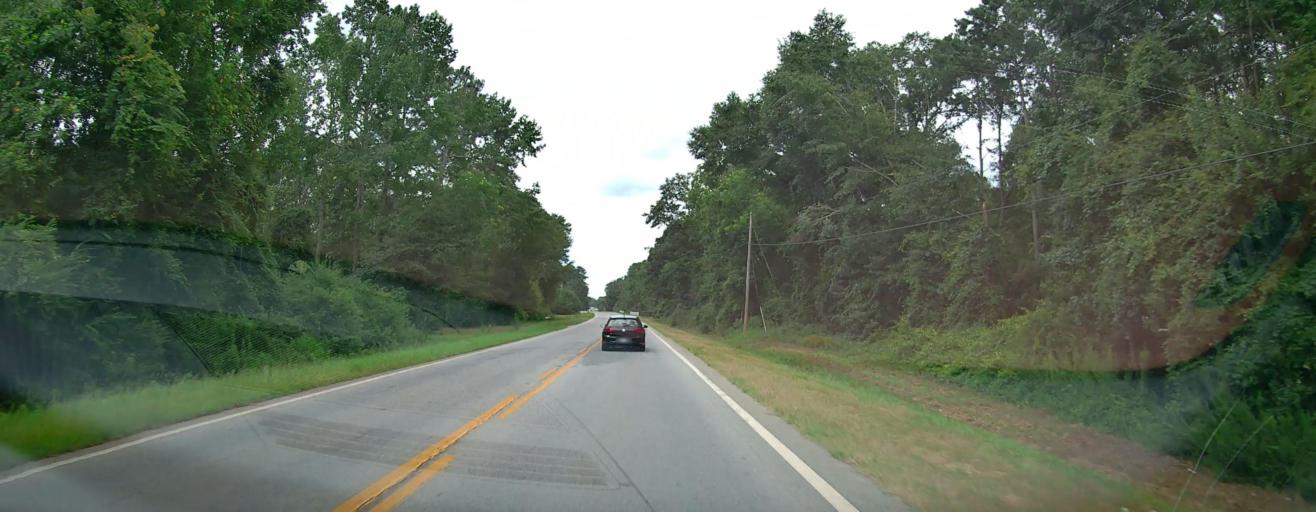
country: US
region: Georgia
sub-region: Macon County
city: Oglethorpe
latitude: 32.2722
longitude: -84.0744
